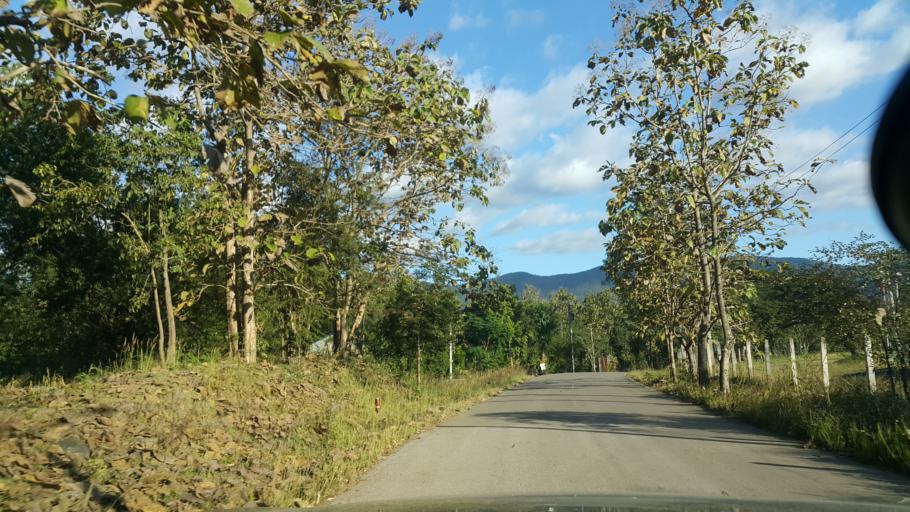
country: TH
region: Chiang Mai
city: Mae On
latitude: 18.7729
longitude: 99.2494
